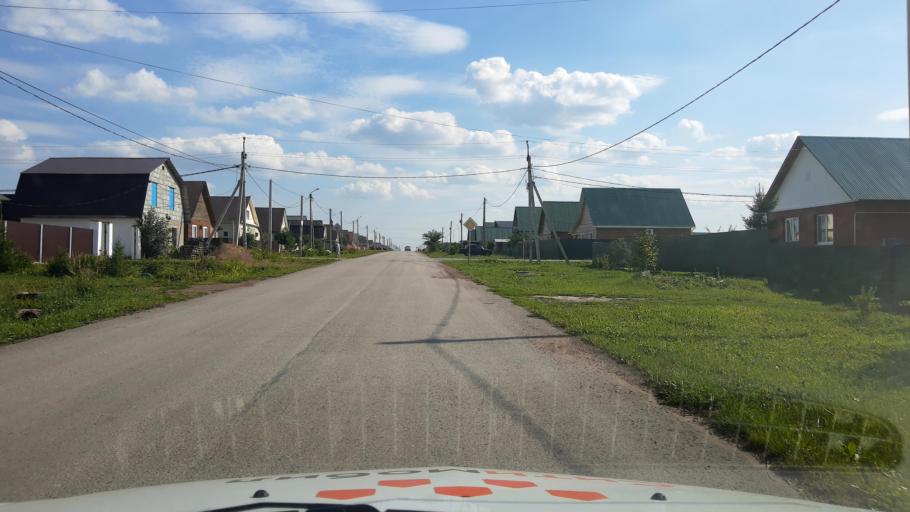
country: RU
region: Bashkortostan
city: Kabakovo
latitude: 54.6558
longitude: 56.2141
